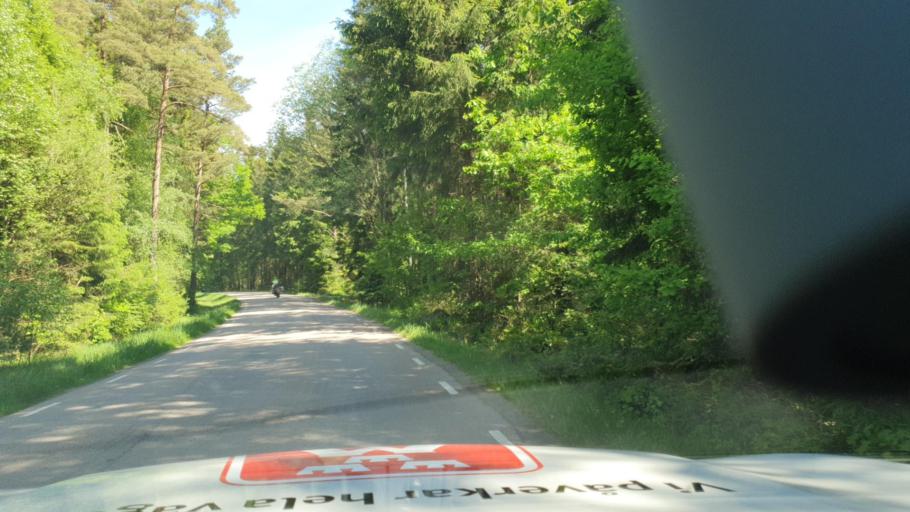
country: SE
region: Vaestra Goetaland
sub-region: Herrljunga Kommun
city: Herrljunga
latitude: 58.0088
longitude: 13.0898
